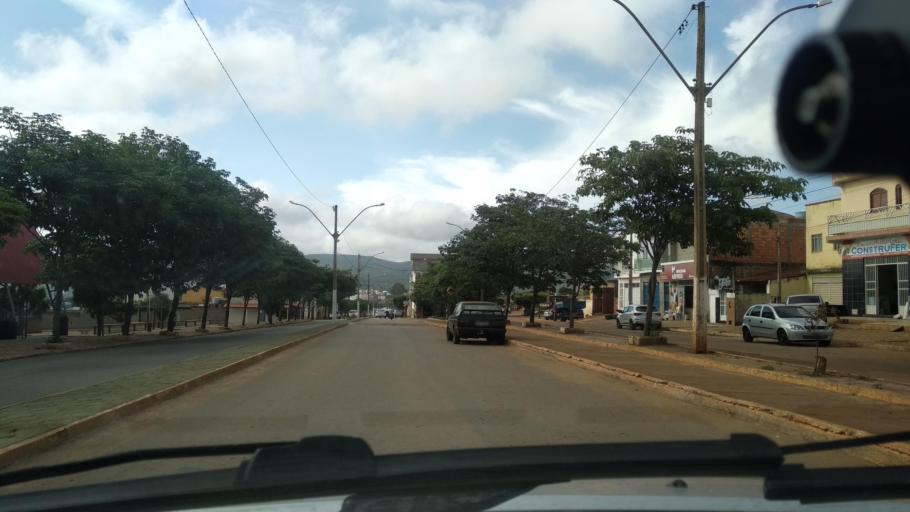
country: BR
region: Bahia
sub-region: Caetite
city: Caetite
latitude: -14.0542
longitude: -42.4843
